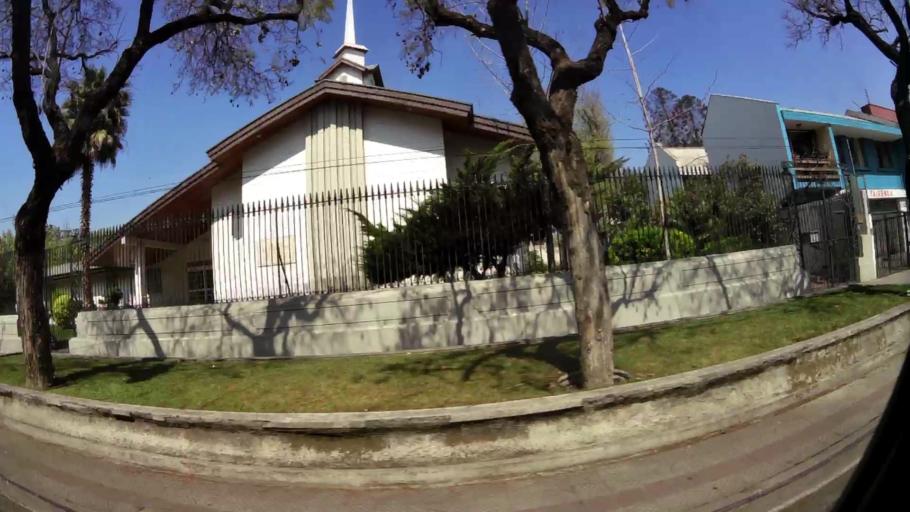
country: CL
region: Santiago Metropolitan
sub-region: Provincia de Santiago
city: Santiago
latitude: -33.4536
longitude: -70.6680
